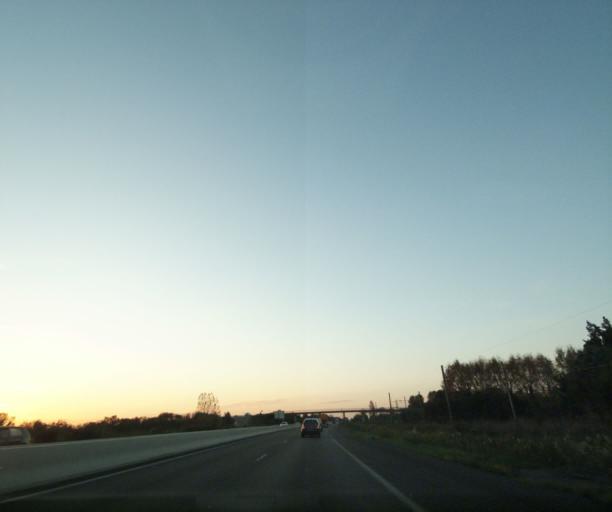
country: FR
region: Provence-Alpes-Cote d'Azur
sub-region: Departement des Bouches-du-Rhone
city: Arles
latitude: 43.6551
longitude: 4.6563
